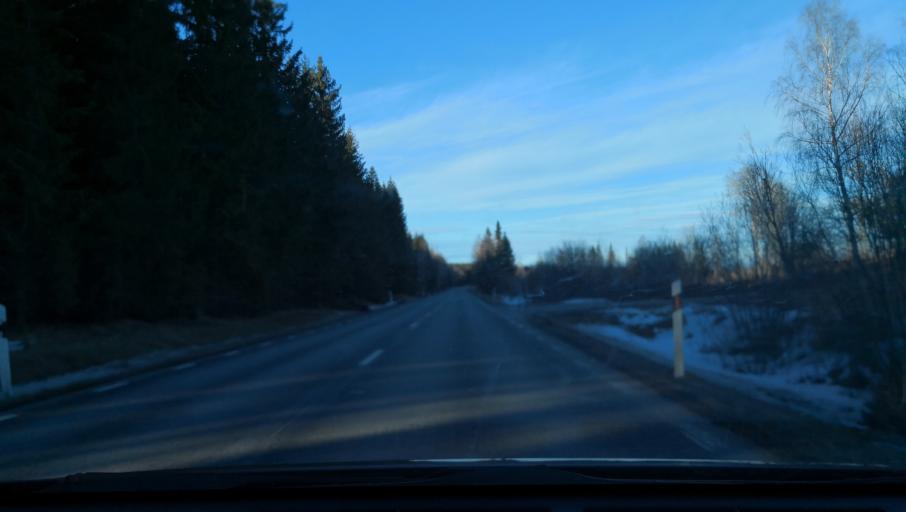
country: SE
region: Uppsala
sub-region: Osthammars Kommun
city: Gimo
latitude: 60.1865
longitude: 18.1902
